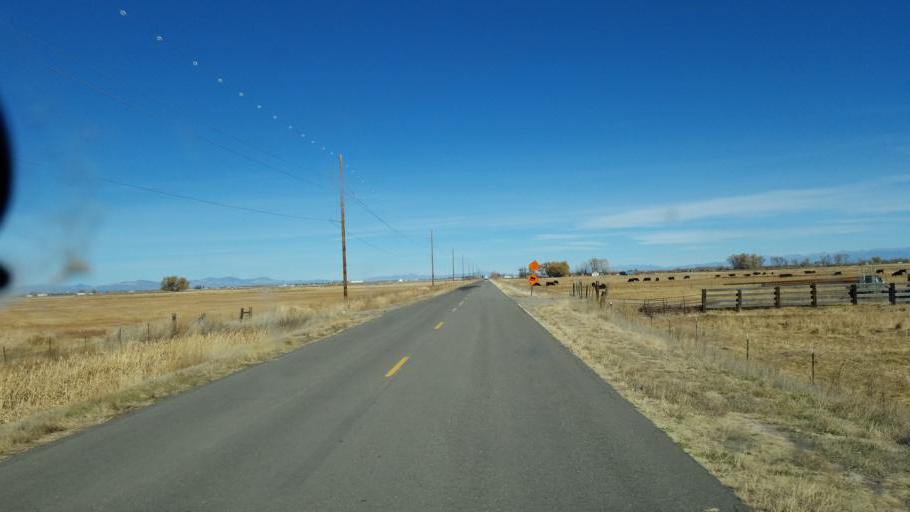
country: US
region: Colorado
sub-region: Rio Grande County
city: Monte Vista
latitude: 37.5167
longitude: -106.0941
